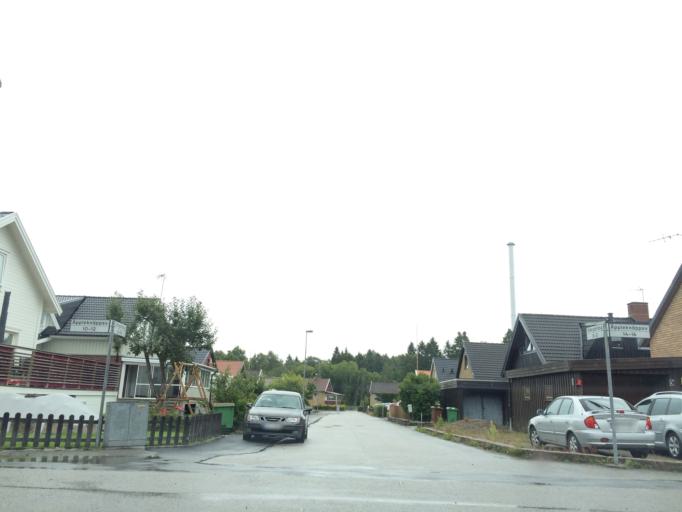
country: SE
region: Vaestra Goetaland
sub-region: Trollhattan
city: Trollhattan
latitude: 58.2801
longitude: 12.2560
